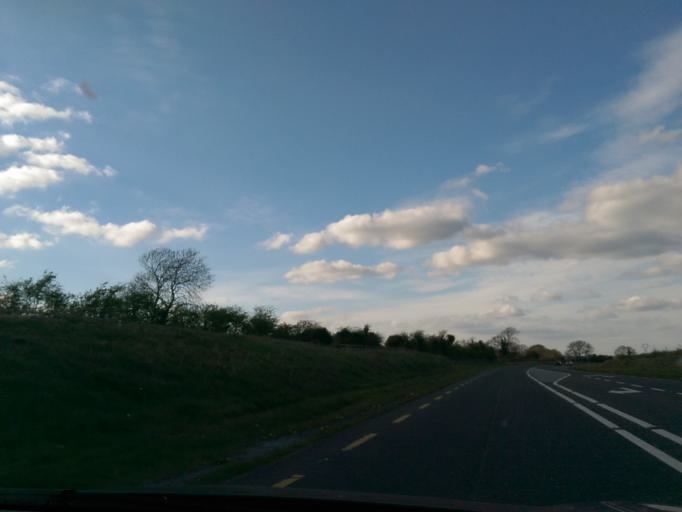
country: IE
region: Connaught
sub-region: County Galway
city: Loughrea
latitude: 53.2316
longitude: -8.5937
